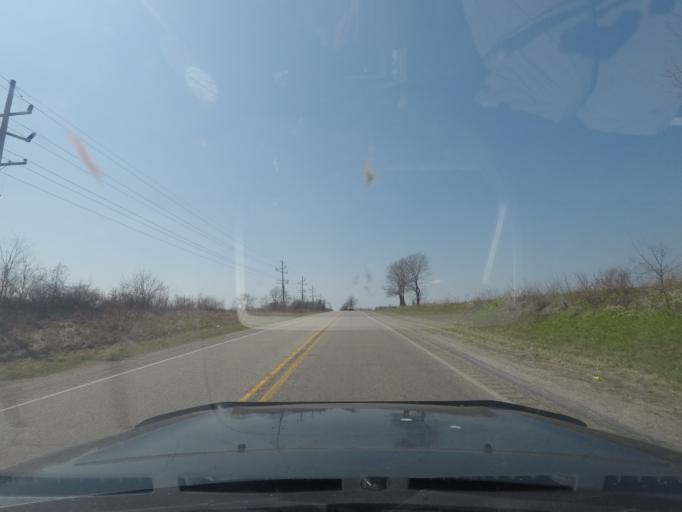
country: US
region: Indiana
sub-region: LaPorte County
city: LaPorte
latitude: 41.5913
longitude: -86.7561
